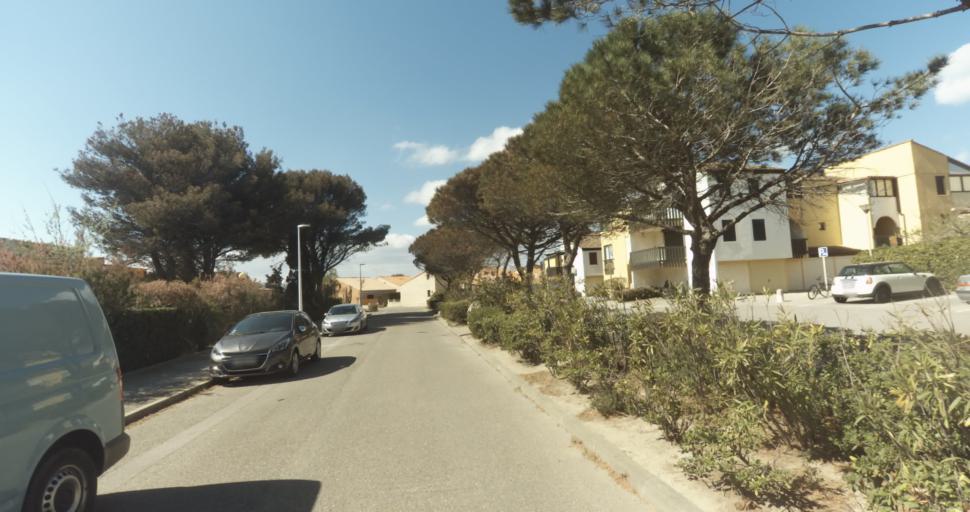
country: FR
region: Languedoc-Roussillon
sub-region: Departement de l'Aude
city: Leucate
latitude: 42.8546
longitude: 3.0425
